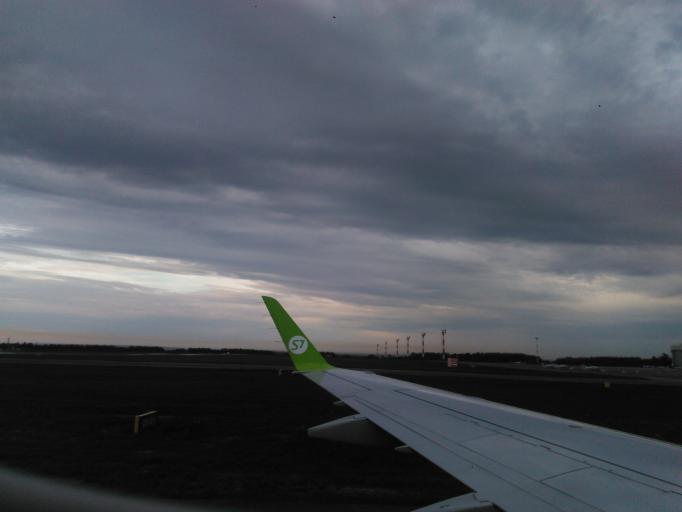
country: RU
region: Tatarstan
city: Yelabuga
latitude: 55.5661
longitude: 52.0976
